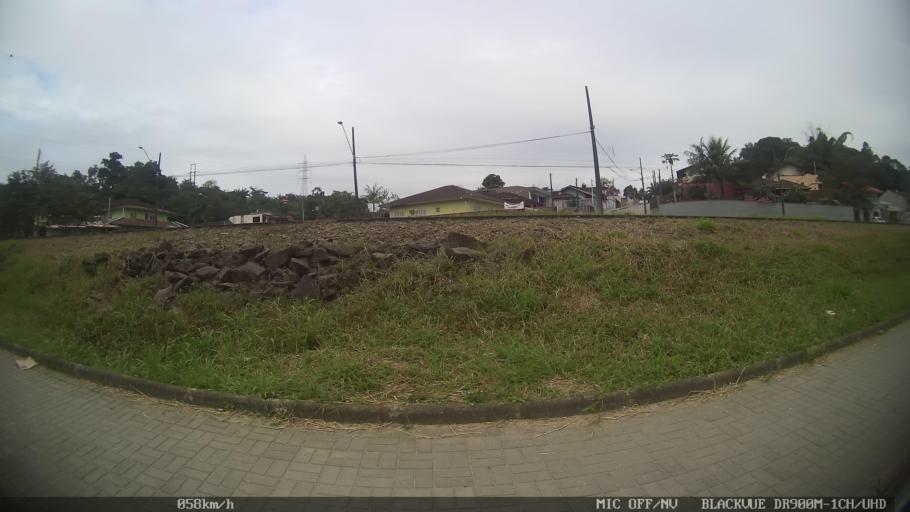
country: BR
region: Santa Catarina
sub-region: Joinville
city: Joinville
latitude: -26.3324
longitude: -48.8752
